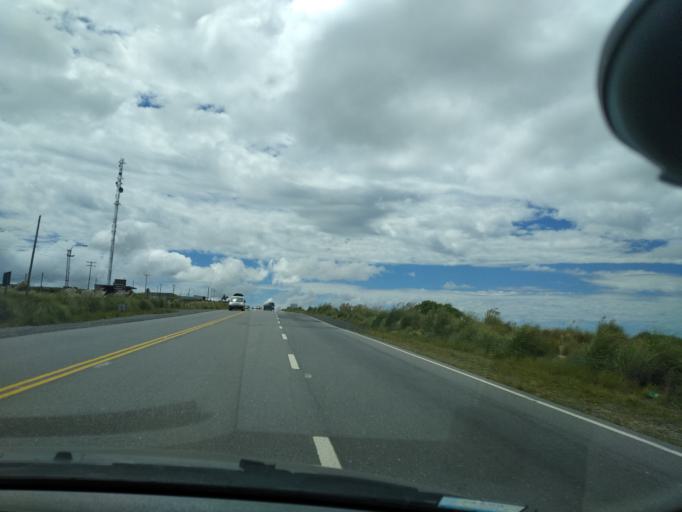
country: AR
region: Cordoba
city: Mina Clavero
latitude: -31.6172
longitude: -64.8757
